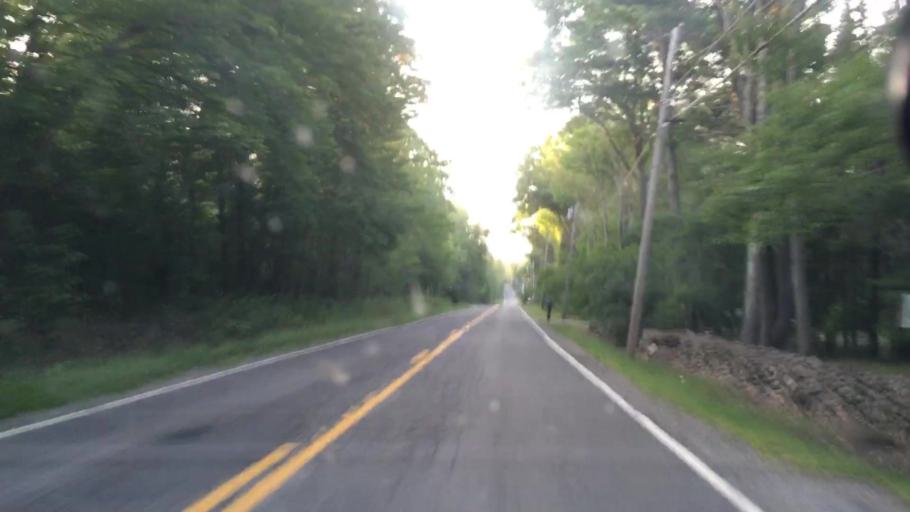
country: US
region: Maine
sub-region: Waldo County
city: Frankfort
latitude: 44.7006
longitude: -68.9457
